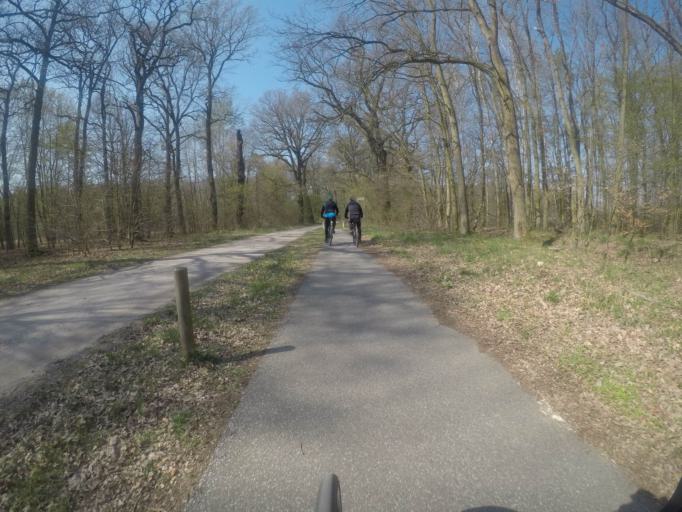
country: DE
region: Brandenburg
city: Hennigsdorf
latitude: 52.6409
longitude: 13.1712
